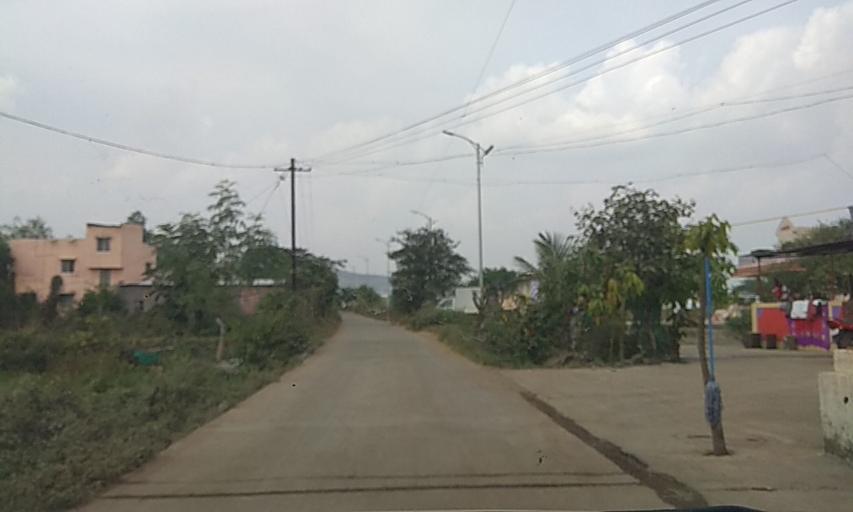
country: IN
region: Maharashtra
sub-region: Pune Division
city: Pimpri
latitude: 18.5777
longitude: 73.7085
